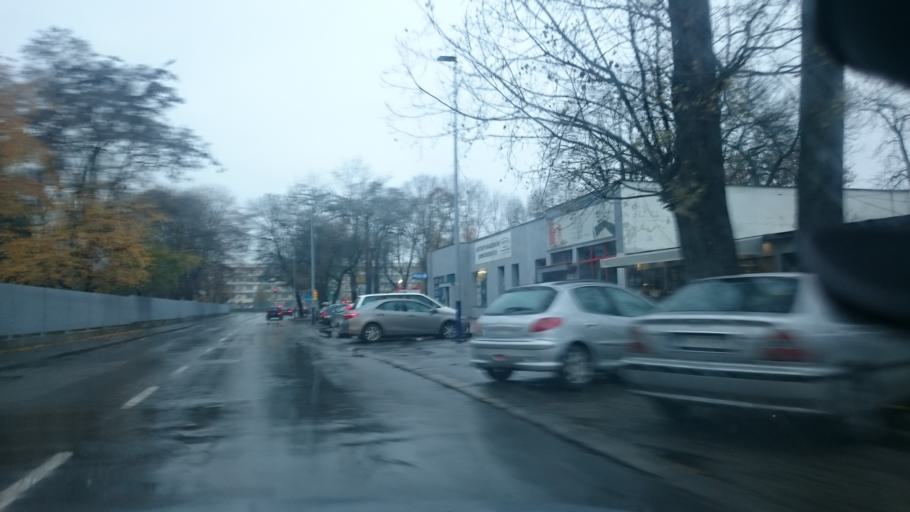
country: PL
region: Lesser Poland Voivodeship
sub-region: Krakow
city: Krakow
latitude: 50.0777
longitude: 19.9521
